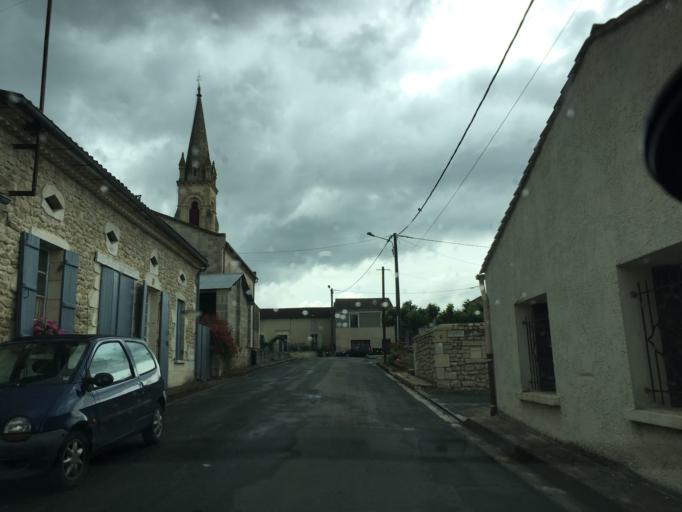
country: FR
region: Aquitaine
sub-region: Departement de la Gironde
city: Vertheuil
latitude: 45.3074
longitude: -0.8357
